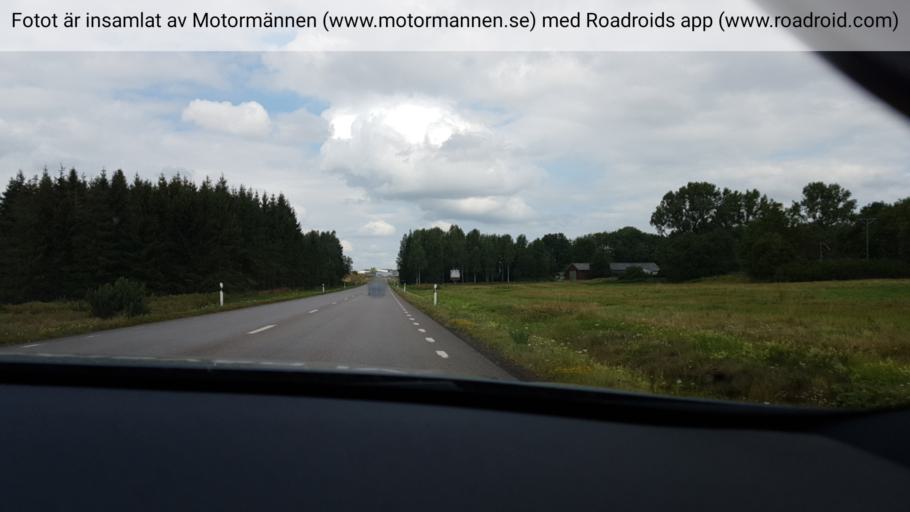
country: SE
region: Vaestra Goetaland
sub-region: Falkopings Kommun
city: Falkoeping
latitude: 58.1423
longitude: 13.5631
